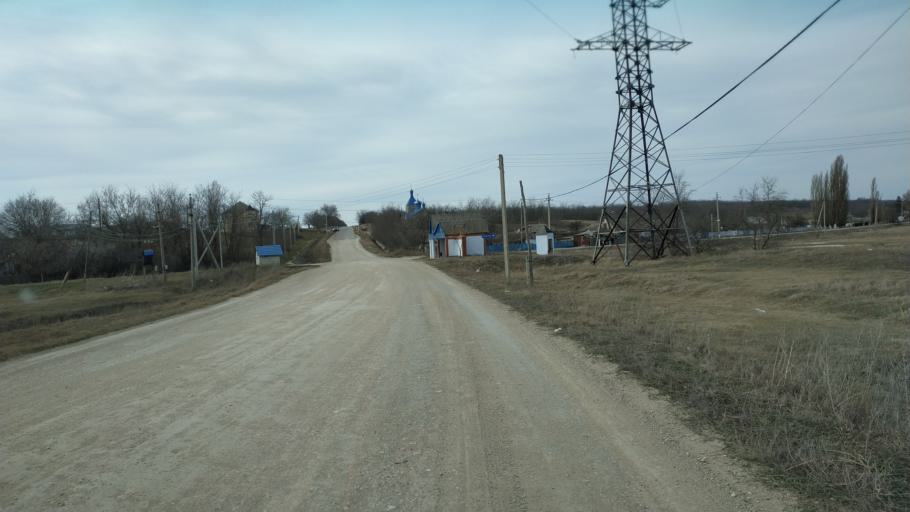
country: RO
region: Vaslui
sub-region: Comuna Dranceni
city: Dranceni
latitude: 46.8598
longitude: 28.2031
